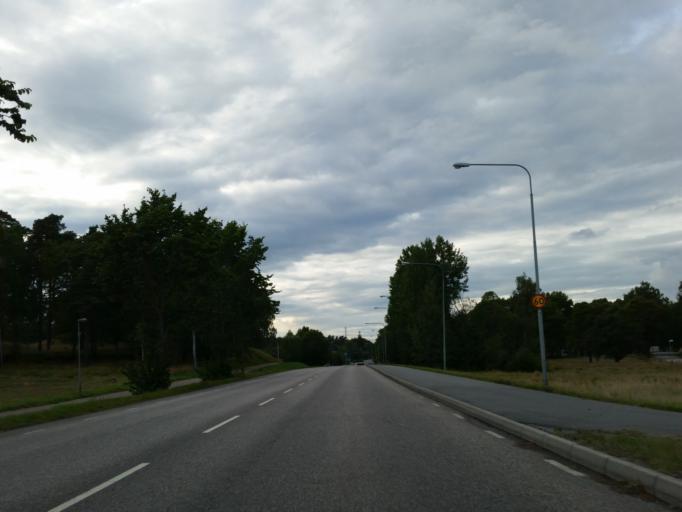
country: SE
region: Stockholm
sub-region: Upplands Vasby Kommun
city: Upplands Vaesby
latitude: 59.5374
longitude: 17.9182
